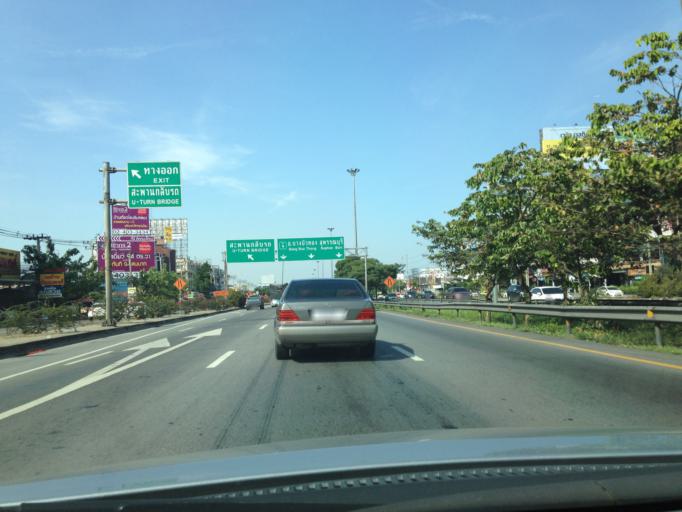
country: TH
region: Nonthaburi
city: Bang Yai
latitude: 13.8466
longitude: 100.4124
